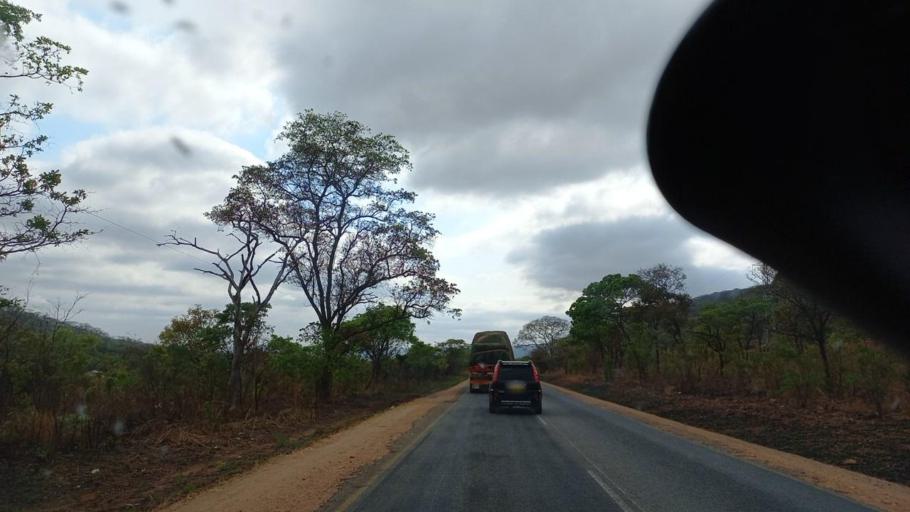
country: ZM
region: Lusaka
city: Chongwe
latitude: -15.1494
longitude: 29.3655
